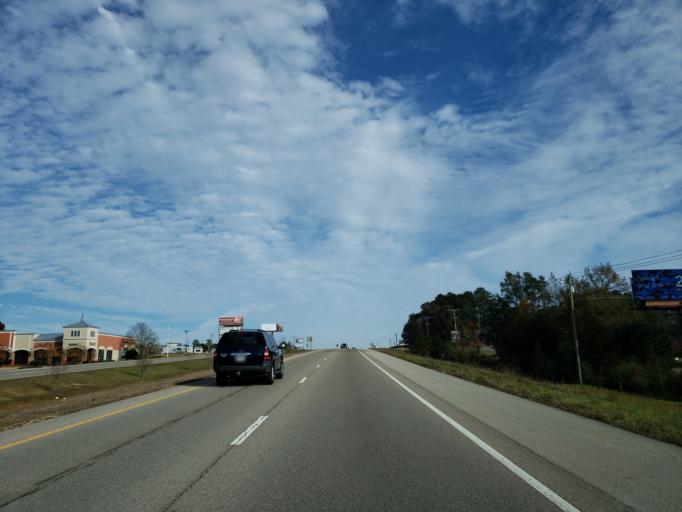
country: US
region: Mississippi
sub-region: Lamar County
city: West Hattiesburg
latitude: 31.3172
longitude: -89.4197
